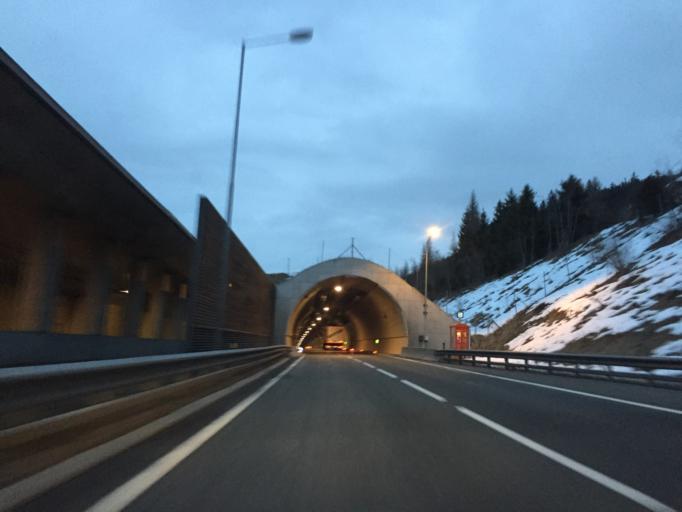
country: AT
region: Salzburg
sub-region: Politischer Bezirk Sankt Johann im Pongau
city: Flachau
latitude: 47.3398
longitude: 13.3959
